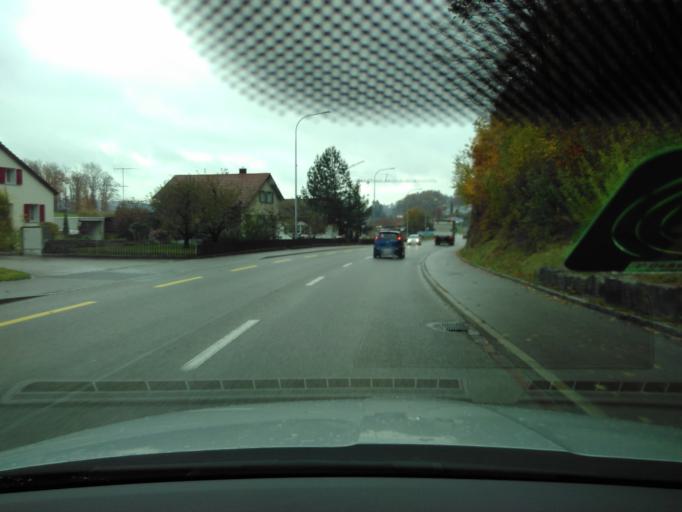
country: CH
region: Aargau
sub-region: Bezirk Zofingen
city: Kirchleerau
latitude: 47.2778
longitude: 8.0615
